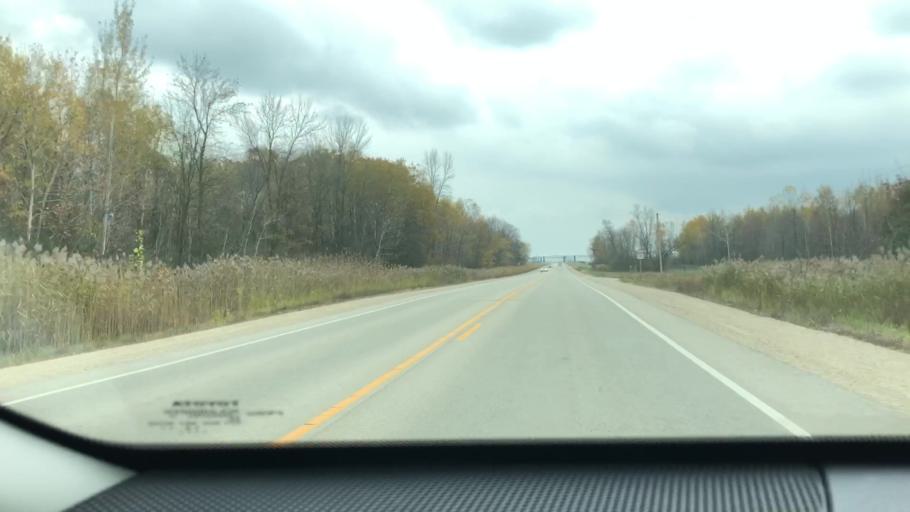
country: US
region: Wisconsin
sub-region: Brown County
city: Oneida
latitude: 44.4988
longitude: -88.1446
